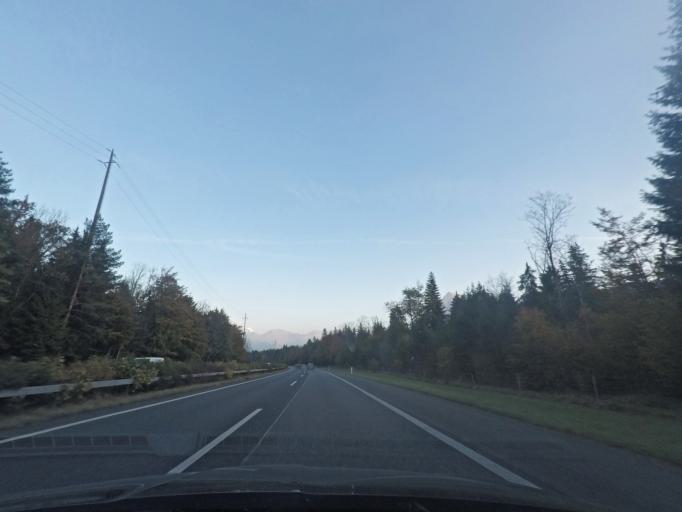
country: CH
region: Bern
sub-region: Thun District
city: Thun
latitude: 46.7172
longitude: 7.6128
